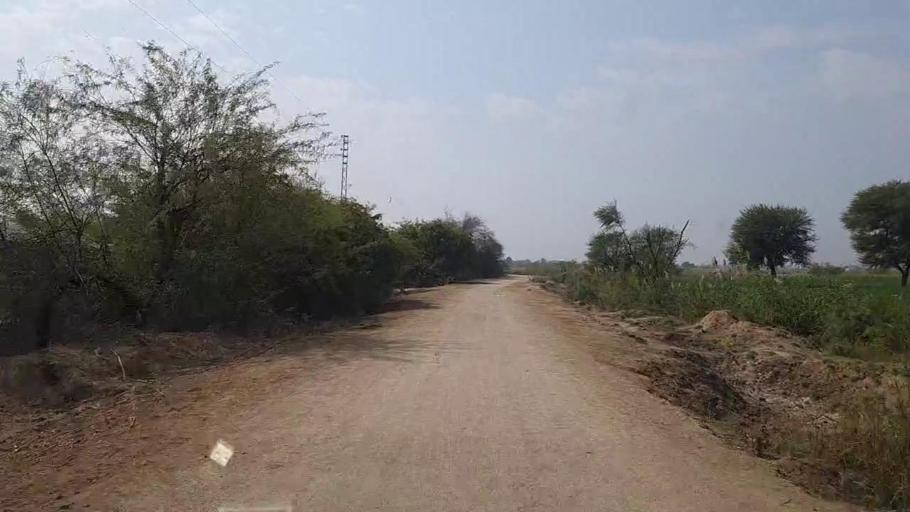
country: PK
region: Sindh
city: Mirwah Gorchani
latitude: 25.3484
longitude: 69.0866
